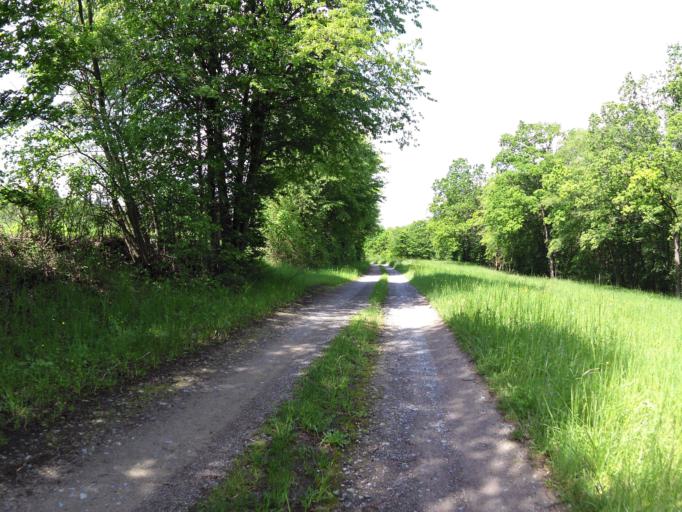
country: DE
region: Bavaria
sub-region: Regierungsbezirk Unterfranken
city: Winterhausen
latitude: 49.7214
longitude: 10.0239
